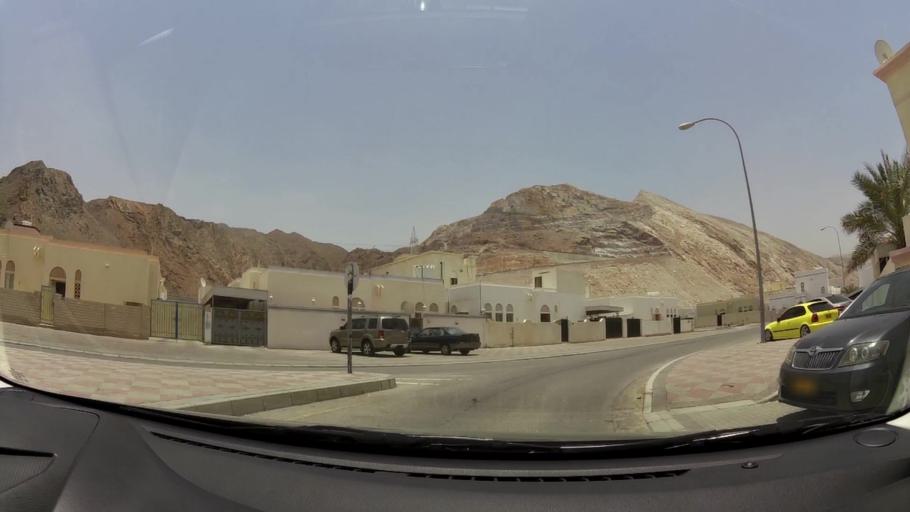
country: OM
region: Muhafazat Masqat
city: Bawshar
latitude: 23.5665
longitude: 58.4258
